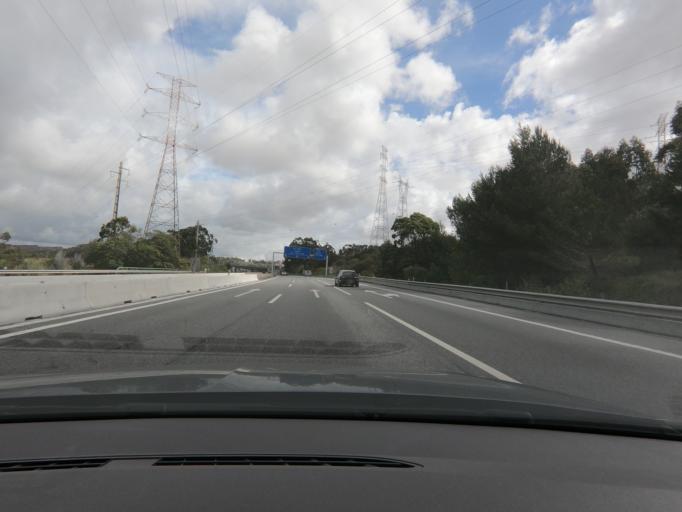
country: PT
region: Lisbon
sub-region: Sintra
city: Belas
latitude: 38.7829
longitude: -9.2443
